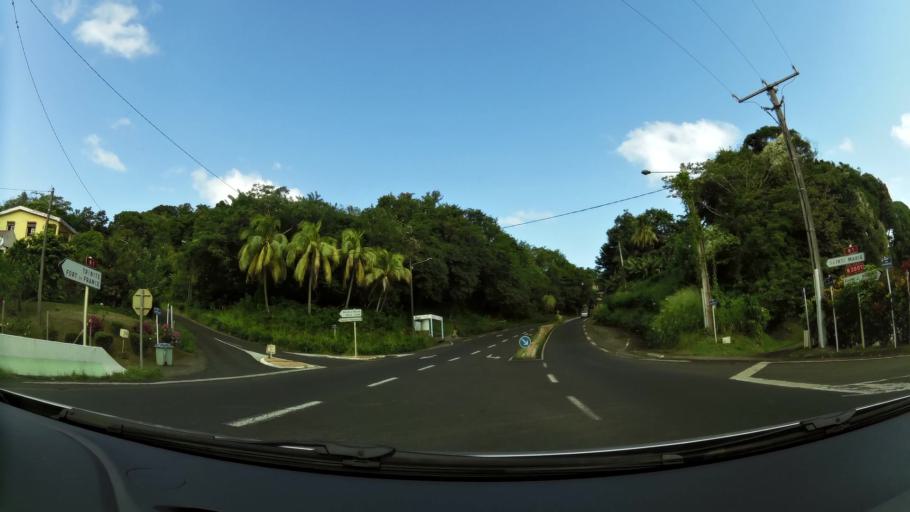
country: MQ
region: Martinique
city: Petite Riviere Salee
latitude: 14.7617
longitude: -60.9819
